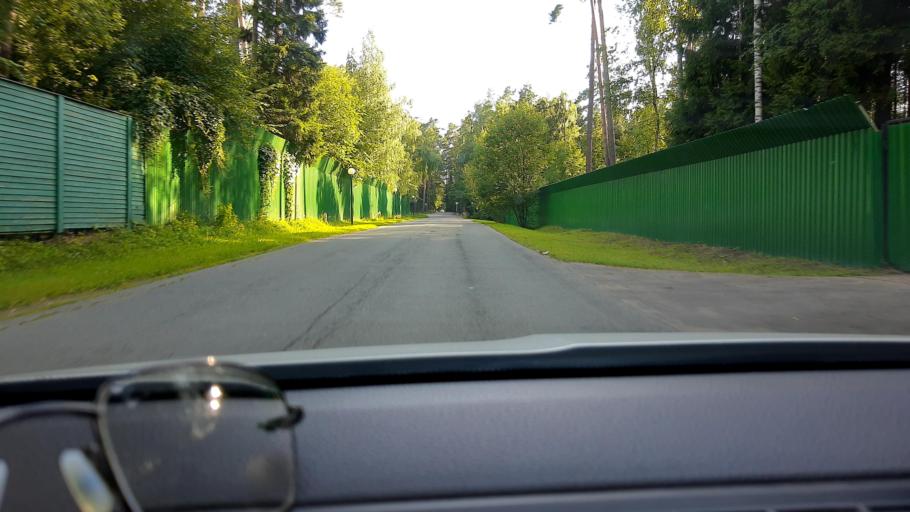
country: RU
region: Moskovskaya
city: Nikolina Gora
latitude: 55.7206
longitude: 36.9617
